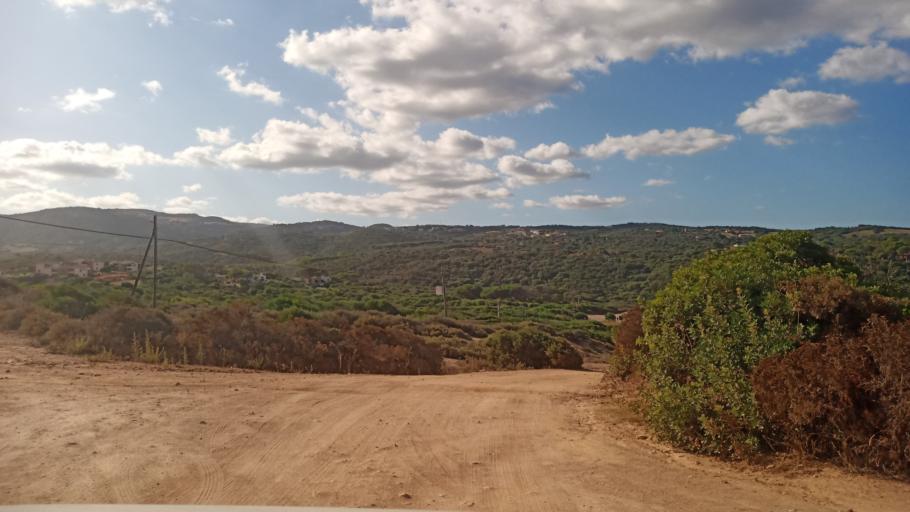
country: IT
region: Sardinia
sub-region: Provincia di Olbia-Tempio
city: Trinita d'Agultu
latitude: 41.0186
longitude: 8.8905
